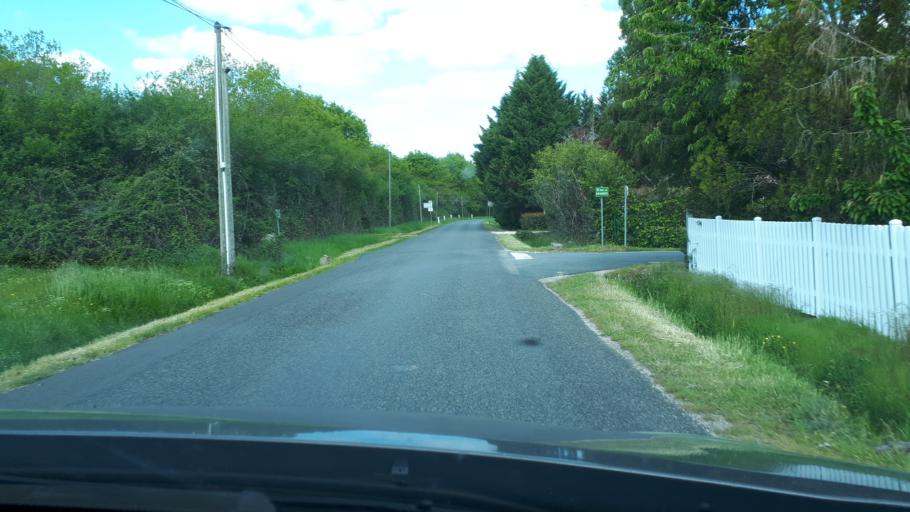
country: FR
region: Centre
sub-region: Departement du Loir-et-Cher
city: Saint-Viatre
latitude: 47.5249
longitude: 1.9249
